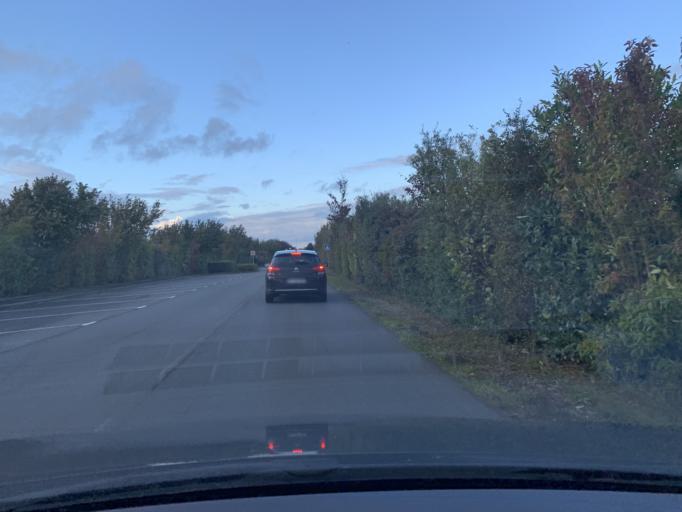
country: FR
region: Nord-Pas-de-Calais
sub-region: Departement du Nord
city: Proville
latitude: 50.1527
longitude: 3.2107
